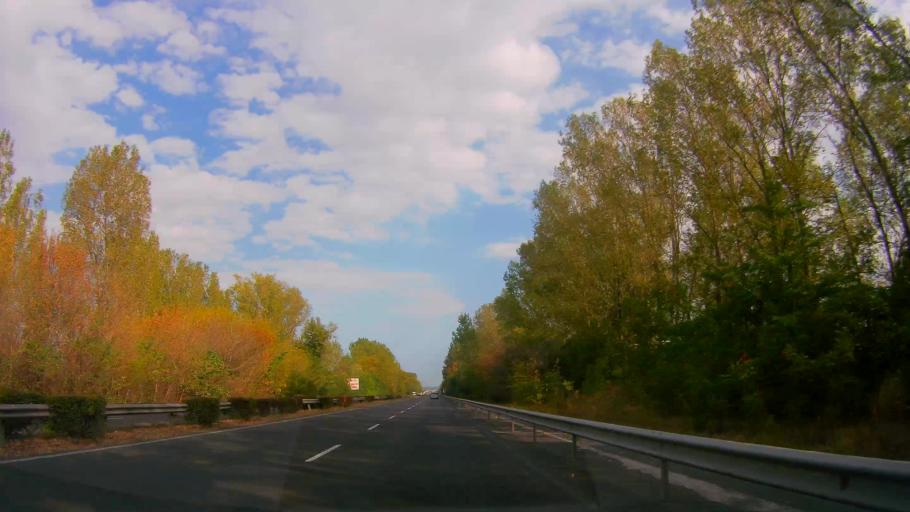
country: BG
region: Burgas
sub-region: Obshtina Burgas
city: Burgas
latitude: 42.4639
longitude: 27.4386
